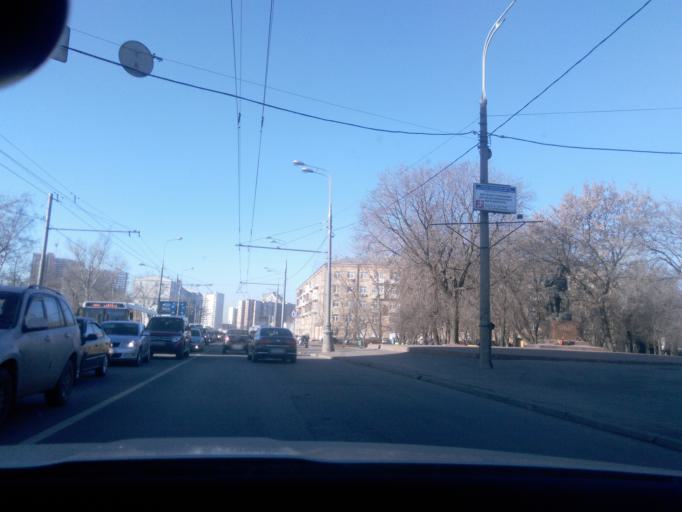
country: RU
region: Moscow
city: Sokol
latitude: 55.7760
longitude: 37.5030
